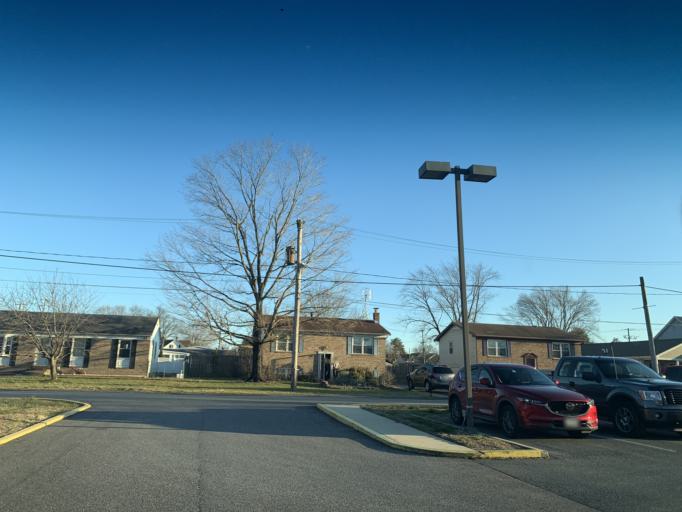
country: US
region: Maryland
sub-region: Cecil County
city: Perryville
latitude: 39.5617
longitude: -76.0760
